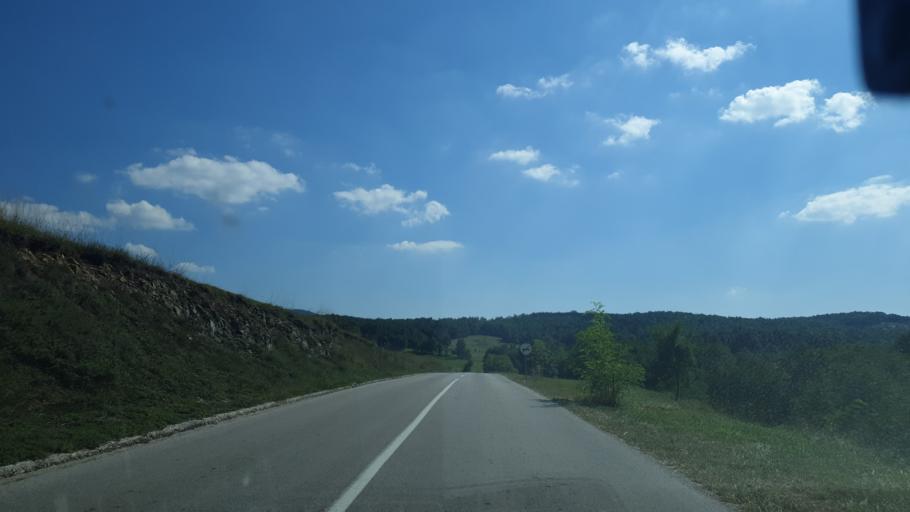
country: RS
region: Central Serbia
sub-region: Zlatiborski Okrug
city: Kosjeric
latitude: 44.0462
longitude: 20.0210
